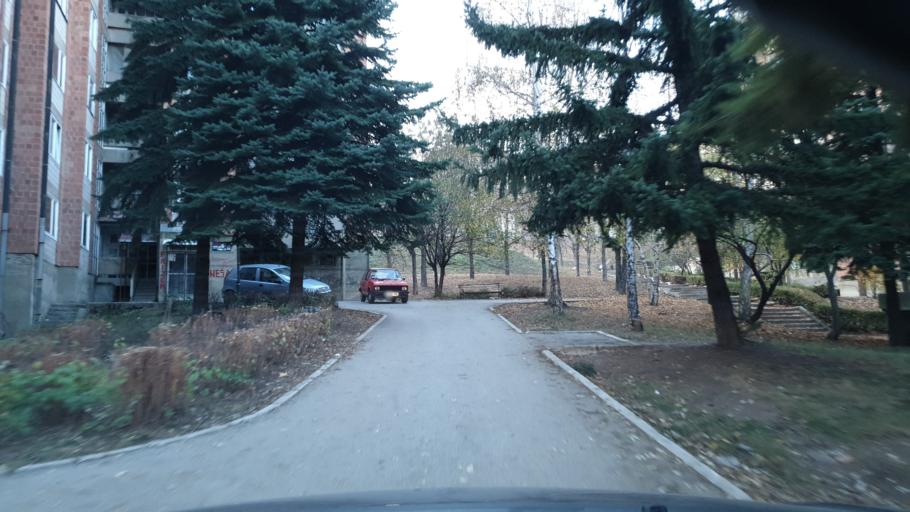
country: RS
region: Central Serbia
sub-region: Borski Okrug
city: Bor
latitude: 44.0552
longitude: 22.0996
